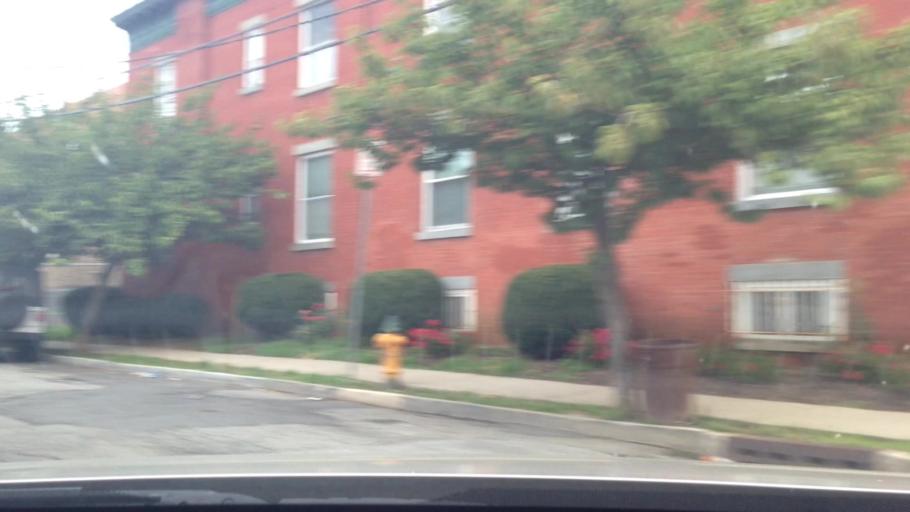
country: US
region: New Jersey
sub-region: Essex County
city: Newark
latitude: 40.7487
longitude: -74.1899
